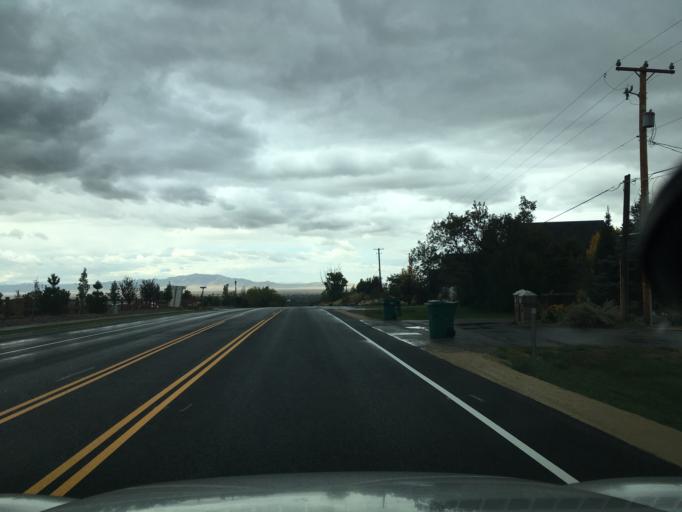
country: US
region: Utah
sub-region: Davis County
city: Fruit Heights
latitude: 41.0658
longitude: -111.9173
